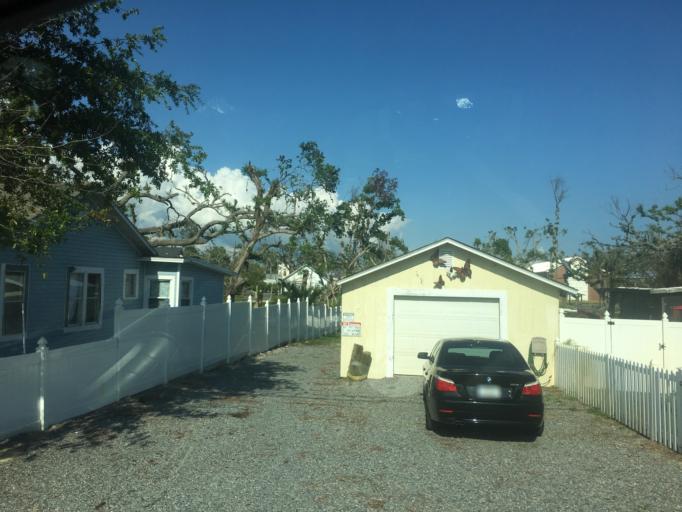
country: US
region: Florida
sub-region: Bay County
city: Cedar Grove
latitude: 30.1524
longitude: -85.6322
